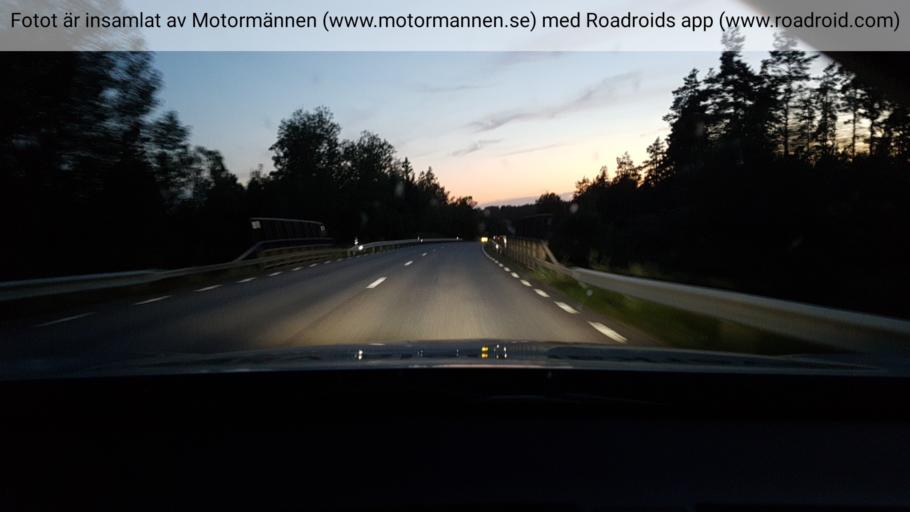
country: SE
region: Vaestra Goetaland
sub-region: Tibro Kommun
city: Tibro
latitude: 58.4537
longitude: 14.2570
